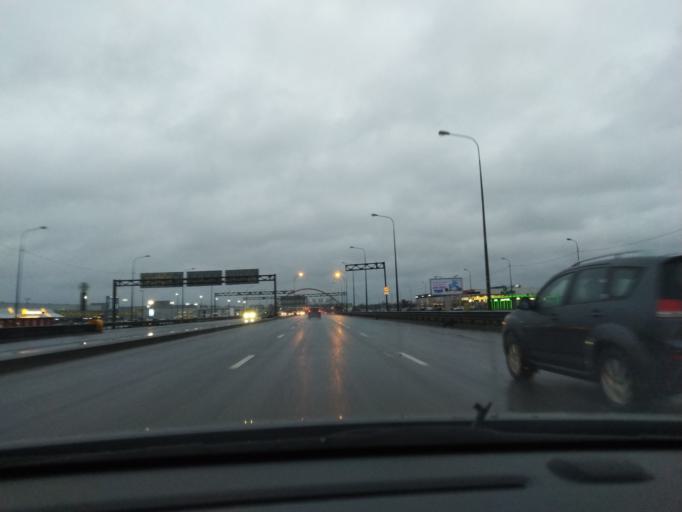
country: RU
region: St.-Petersburg
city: Sosnovaya Polyana
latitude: 59.8046
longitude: 30.1624
